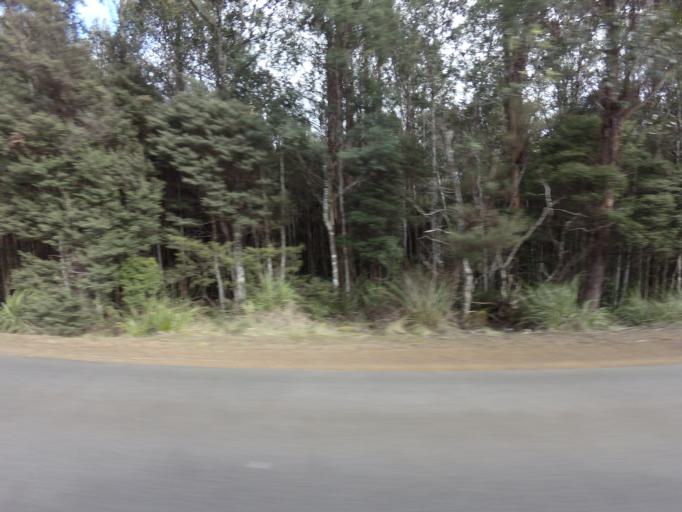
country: AU
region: Tasmania
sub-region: Huon Valley
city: Geeveston
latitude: -43.3712
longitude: 146.9573
